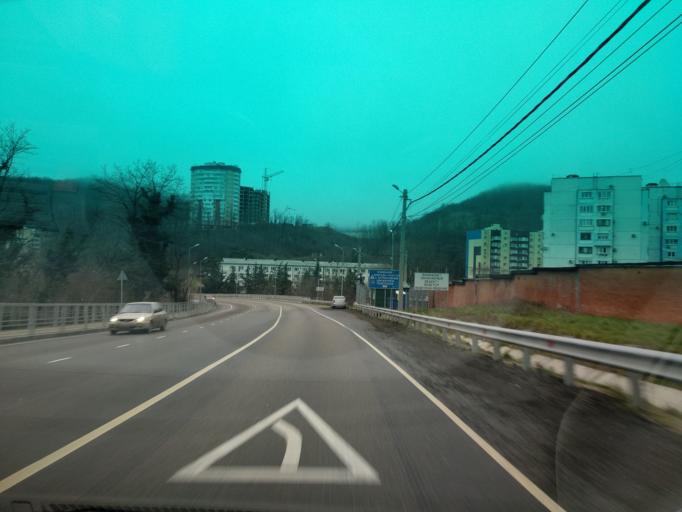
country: RU
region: Krasnodarskiy
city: Tuapse
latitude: 44.1153
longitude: 39.0687
